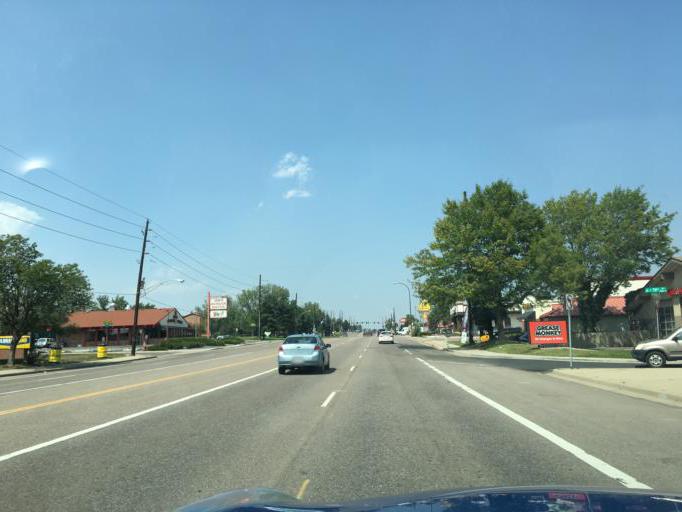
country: US
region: Colorado
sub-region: Adams County
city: Westminster
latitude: 39.8380
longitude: -105.0532
